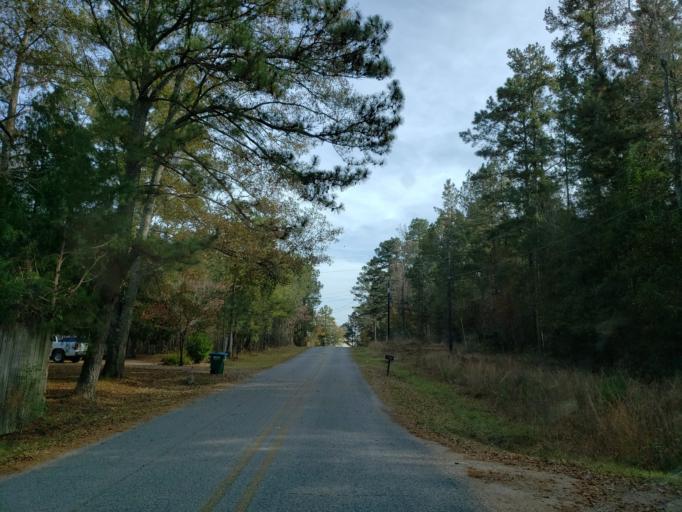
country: US
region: Mississippi
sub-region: Forrest County
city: Rawls Springs
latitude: 31.3718
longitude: -89.3628
